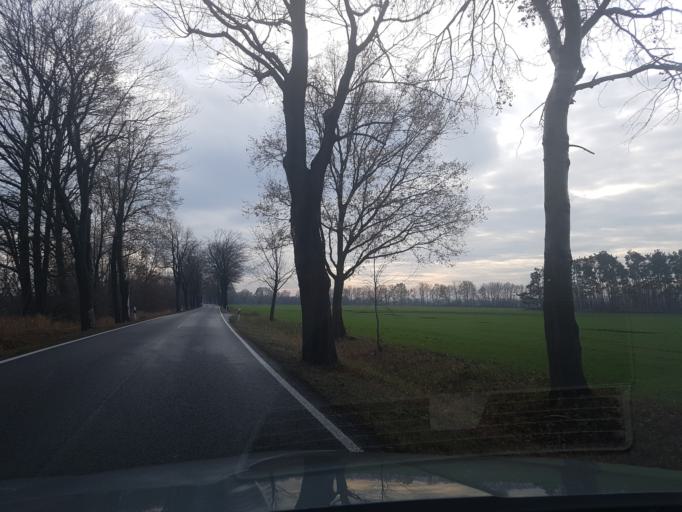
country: DE
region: Brandenburg
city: Plessa
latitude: 51.4403
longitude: 13.6227
